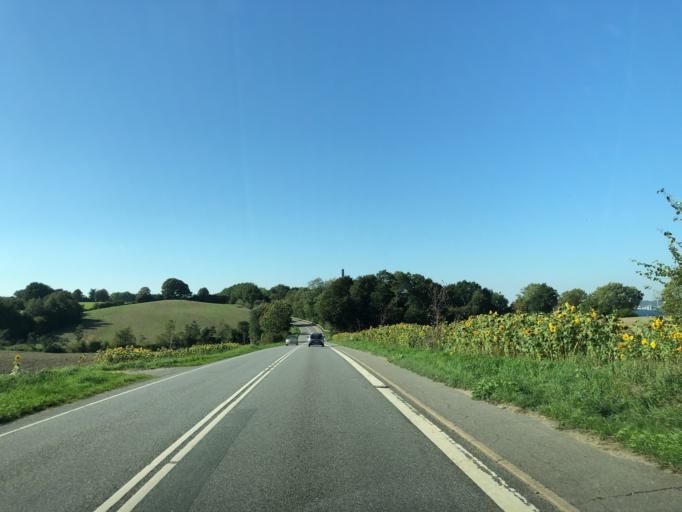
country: DK
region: South Denmark
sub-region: Aabenraa Kommune
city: Aabenraa
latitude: 55.0155
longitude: 9.4729
